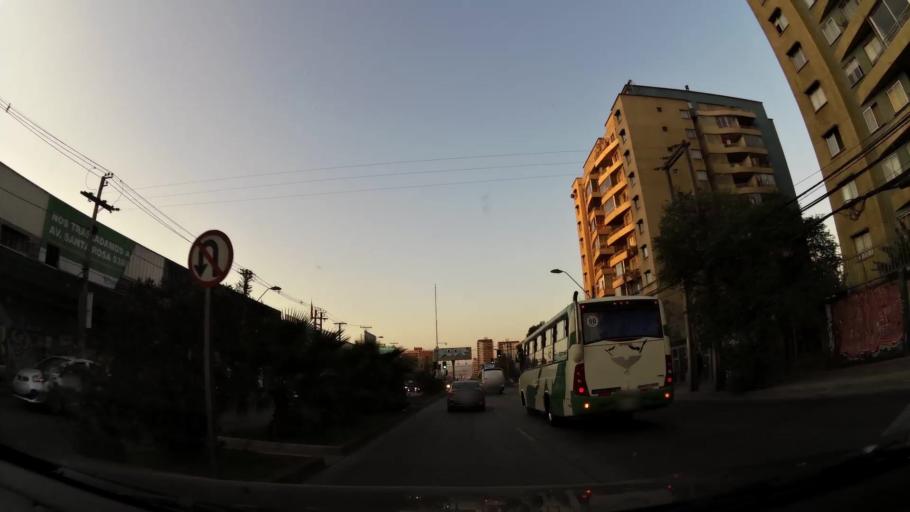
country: CL
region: Santiago Metropolitan
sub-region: Provincia de Santiago
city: Santiago
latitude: -33.5135
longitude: -70.6577
